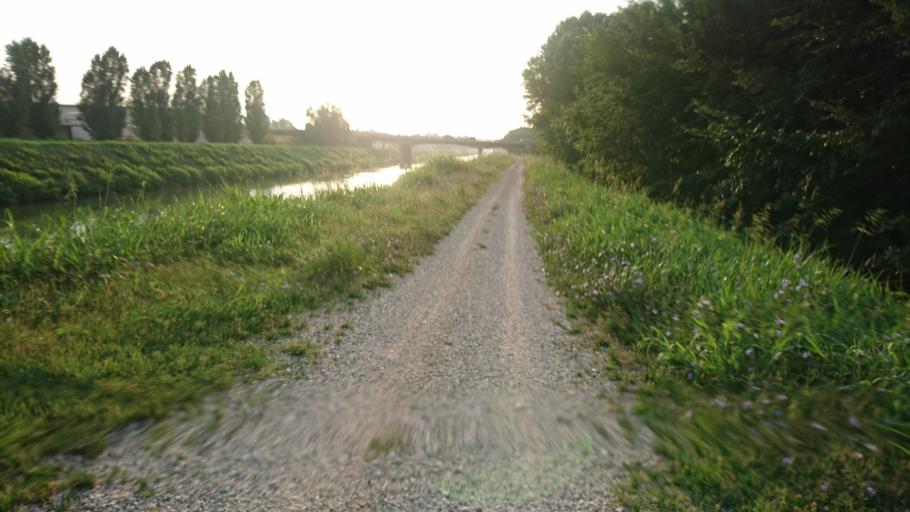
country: IT
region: Veneto
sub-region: Provincia di Padova
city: Noventa
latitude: 45.4066
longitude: 11.9296
